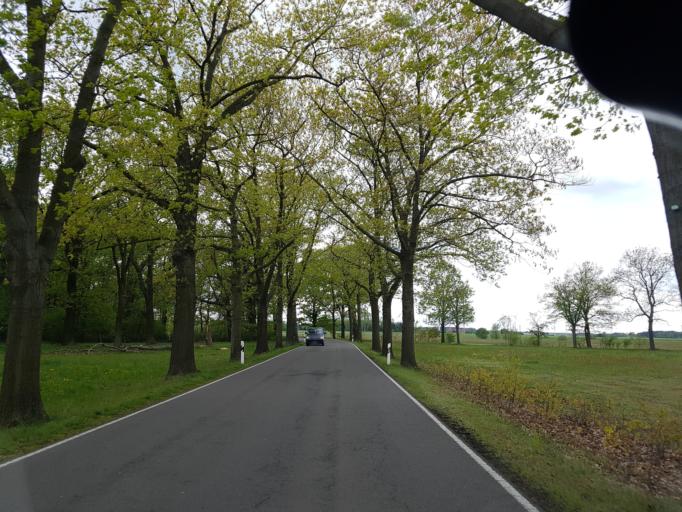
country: DE
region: Brandenburg
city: Bronkow
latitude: 51.6101
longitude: 13.9034
